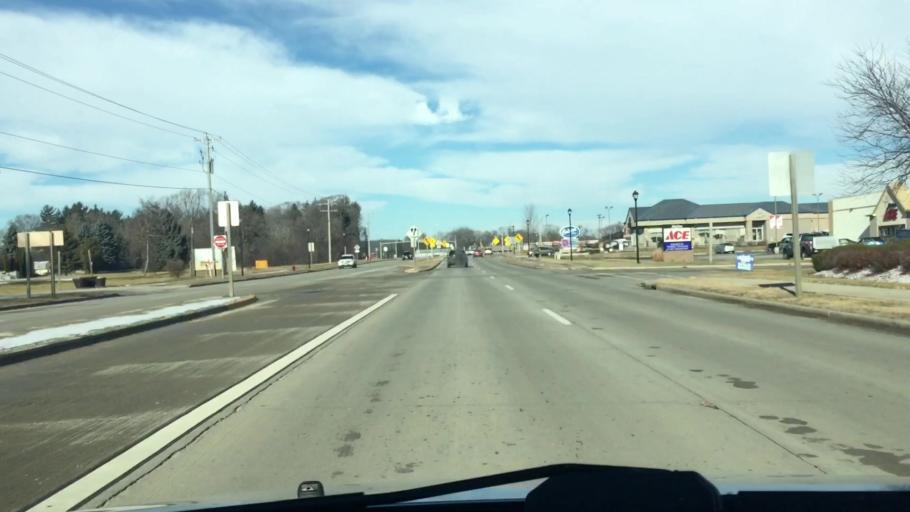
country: US
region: Wisconsin
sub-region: Waukesha County
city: Mukwonago
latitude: 42.8771
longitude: -88.3394
